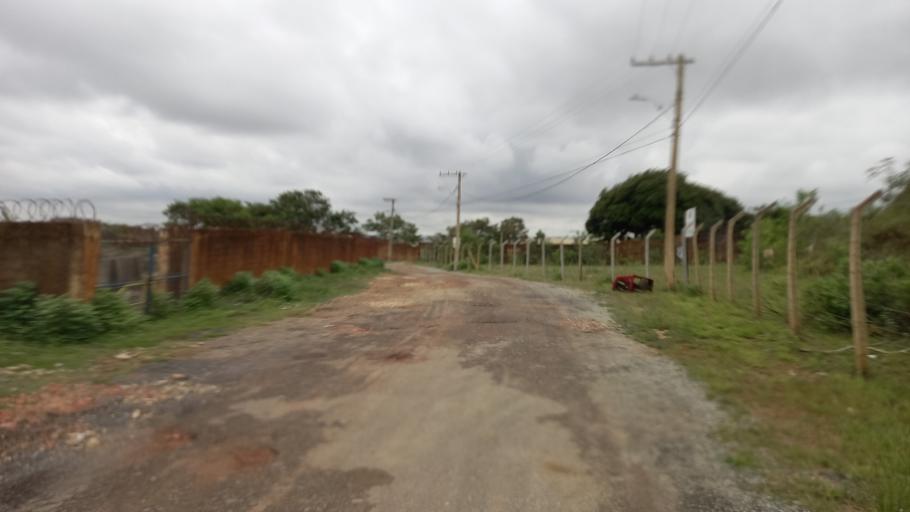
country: BR
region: Minas Gerais
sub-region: Belo Horizonte
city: Belo Horizonte
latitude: -19.9198
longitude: -43.8873
